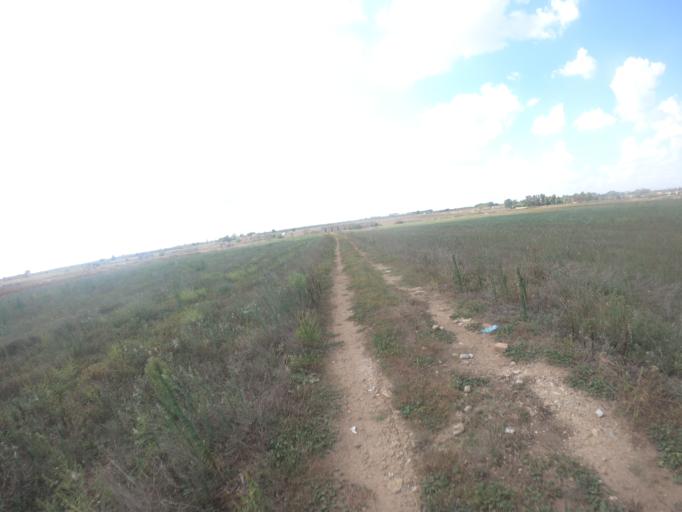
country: IT
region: Apulia
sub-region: Provincia di Lecce
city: Ruffano
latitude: 39.9533
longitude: 18.2600
